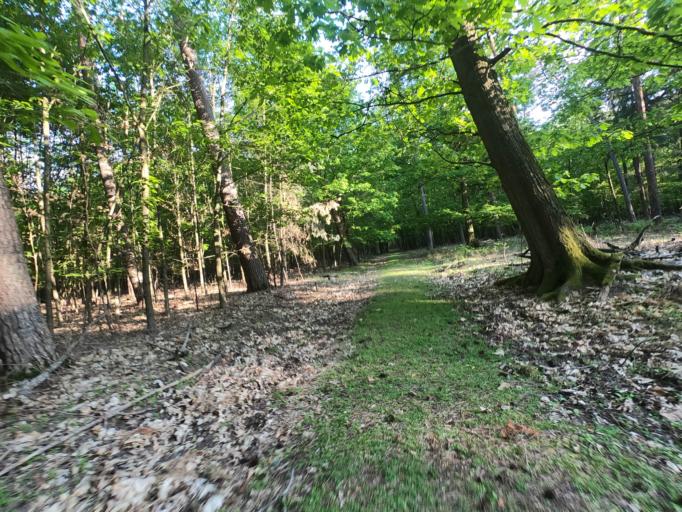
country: DE
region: Hesse
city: Morfelden-Walldorf
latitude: 50.0087
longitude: 8.5385
